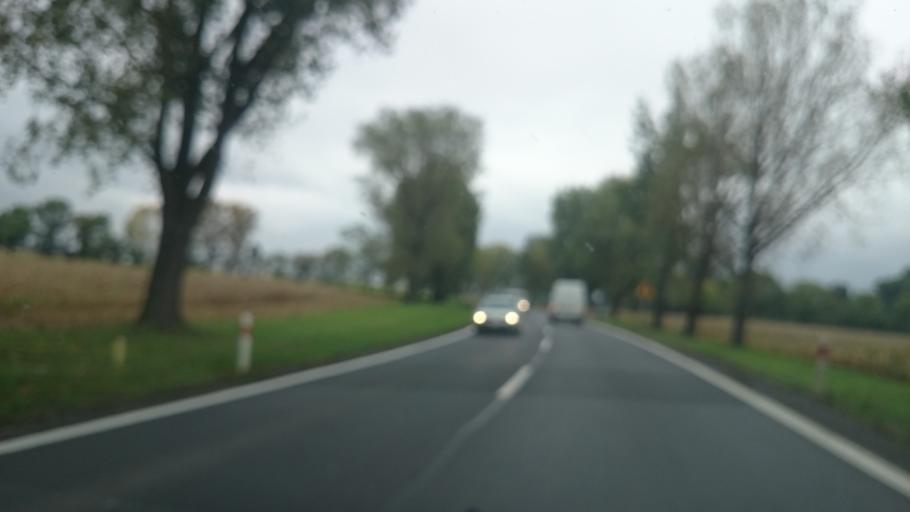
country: PL
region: Lower Silesian Voivodeship
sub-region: Powiat wroclawski
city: Kobierzyce
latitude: 50.9483
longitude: 16.9084
